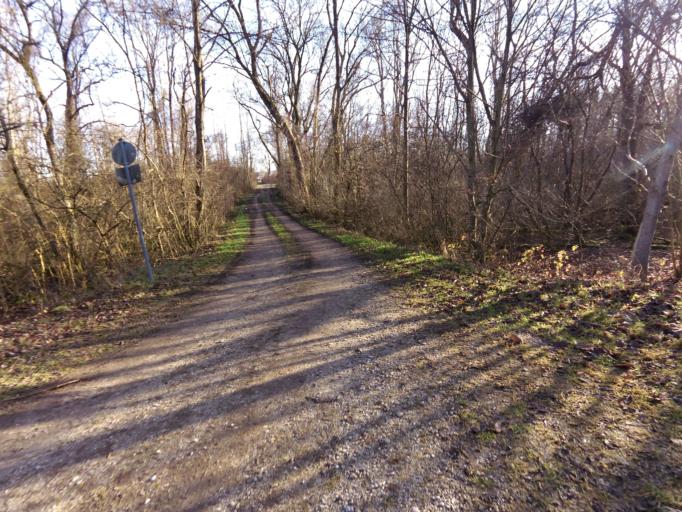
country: DE
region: Bavaria
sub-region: Upper Bavaria
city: Moosburg
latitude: 48.4746
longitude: 11.9573
